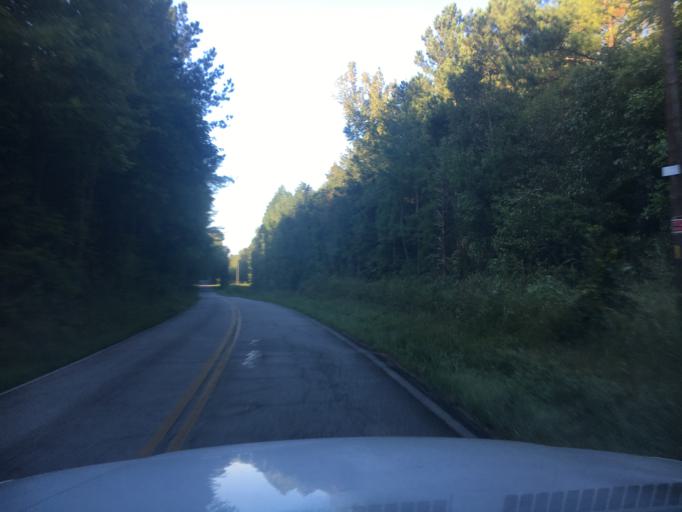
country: US
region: South Carolina
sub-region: Spartanburg County
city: Woodruff
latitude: 34.6801
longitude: -81.9612
